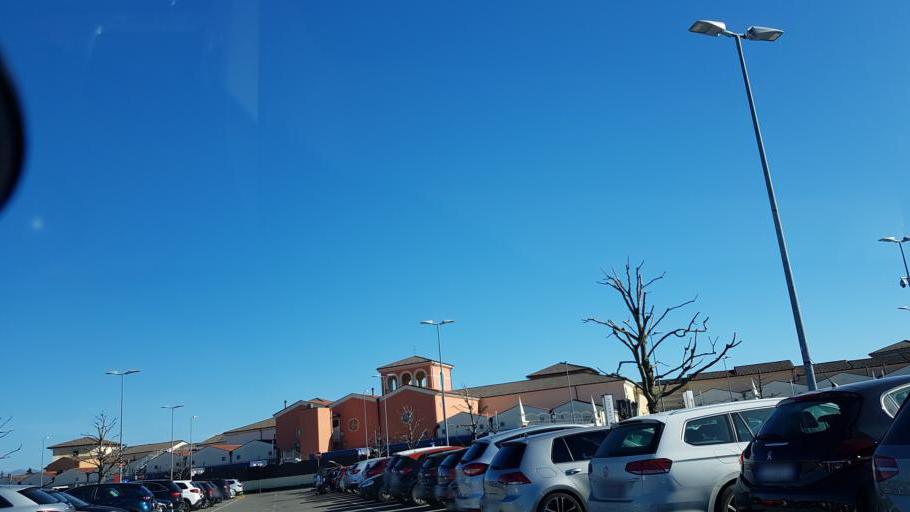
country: IT
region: Piedmont
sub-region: Provincia di Alessandria
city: Serravalle Scrivia
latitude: 44.7375
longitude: 8.8350
